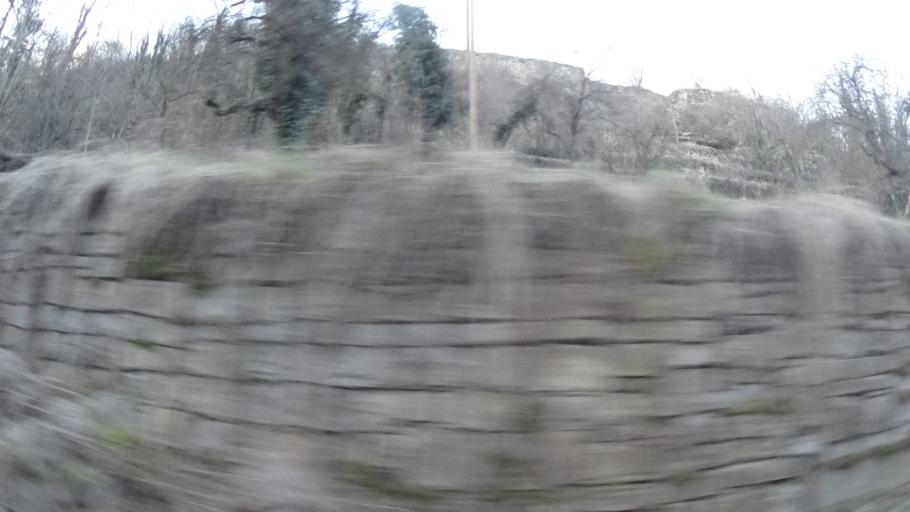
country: DE
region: Baden-Wuerttemberg
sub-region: Regierungsbezirk Stuttgart
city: Markgroningen
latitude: 48.9036
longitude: 9.0715
